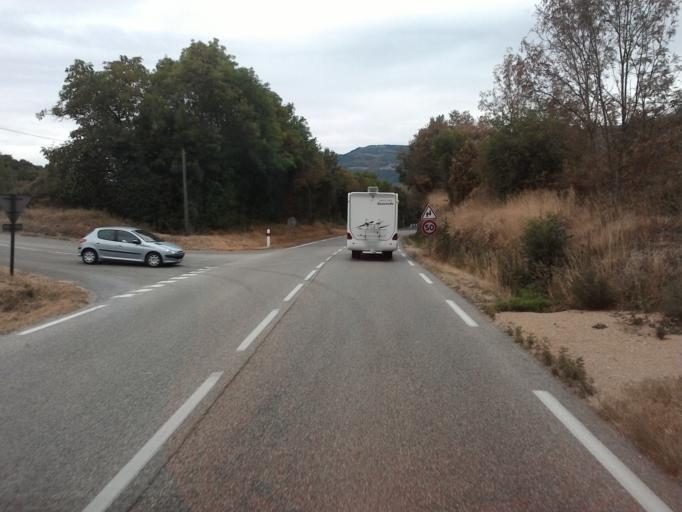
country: FR
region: Rhone-Alpes
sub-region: Departement de l'Isere
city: Porcieu-Amblagnieu
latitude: 45.8370
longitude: 5.4114
